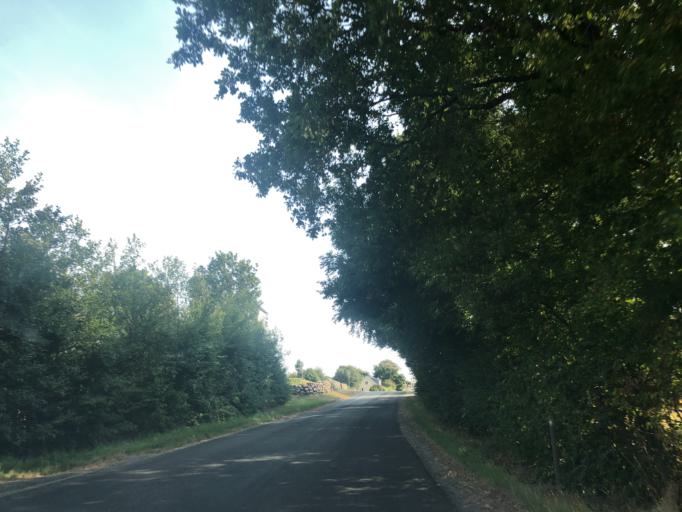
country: DK
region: Central Jutland
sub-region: Skive Kommune
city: Skive
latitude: 56.7206
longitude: 9.0226
